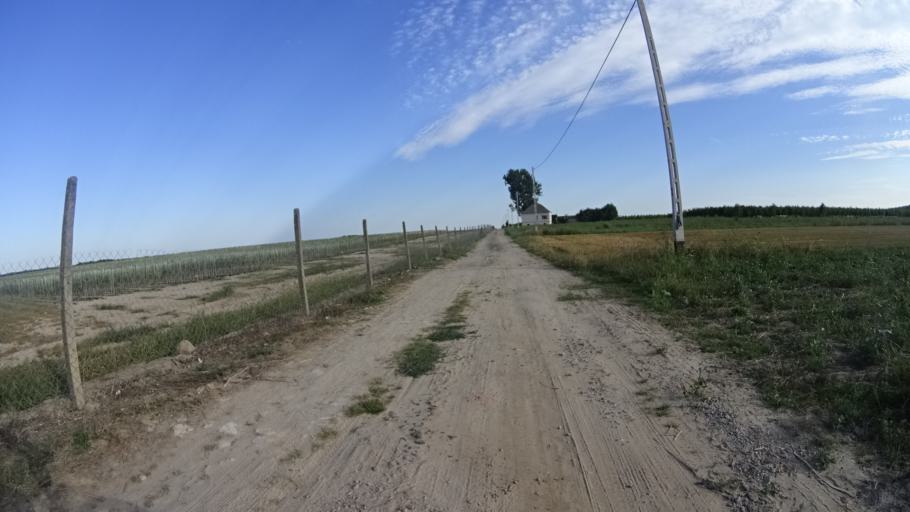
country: PL
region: Masovian Voivodeship
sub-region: Powiat bialobrzeski
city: Wysmierzyce
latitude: 51.6809
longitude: 20.8156
